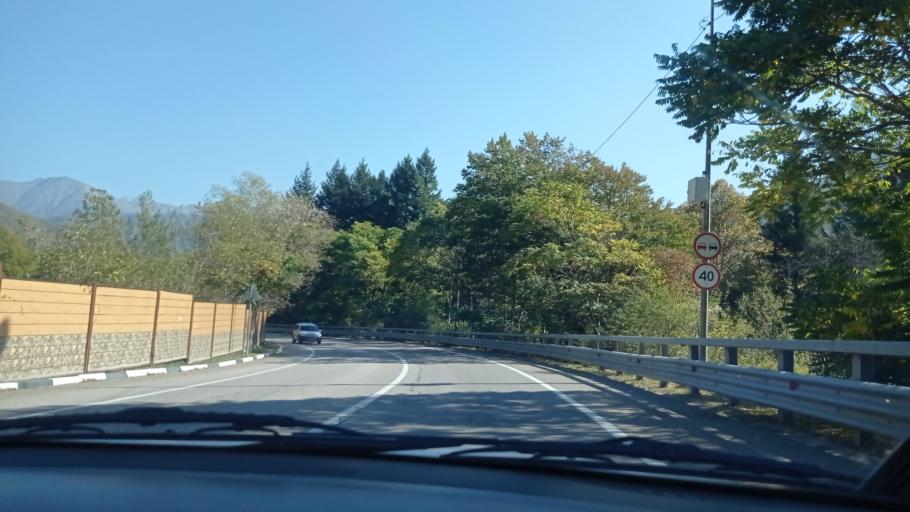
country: RU
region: Krasnodarskiy
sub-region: Sochi City
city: Krasnaya Polyana
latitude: 43.6823
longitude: 40.2216
